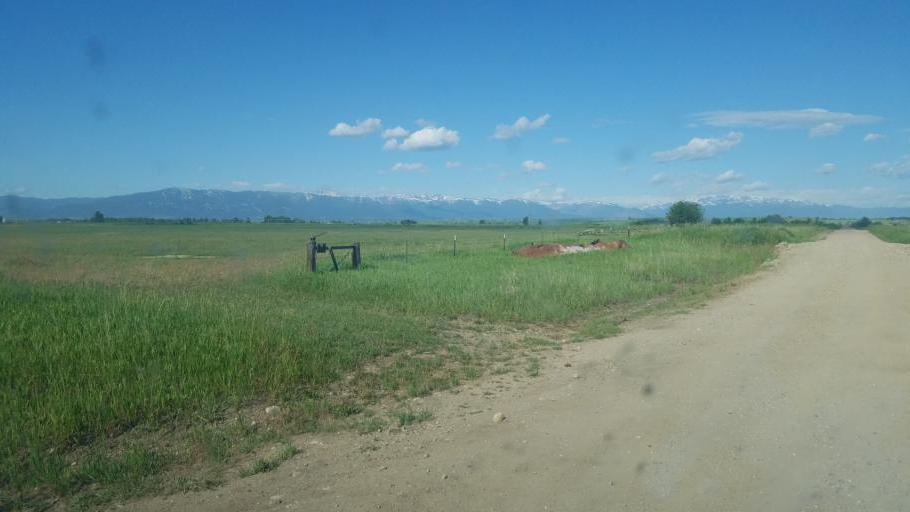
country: US
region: Montana
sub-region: Carbon County
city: Red Lodge
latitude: 45.3442
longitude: -109.1573
